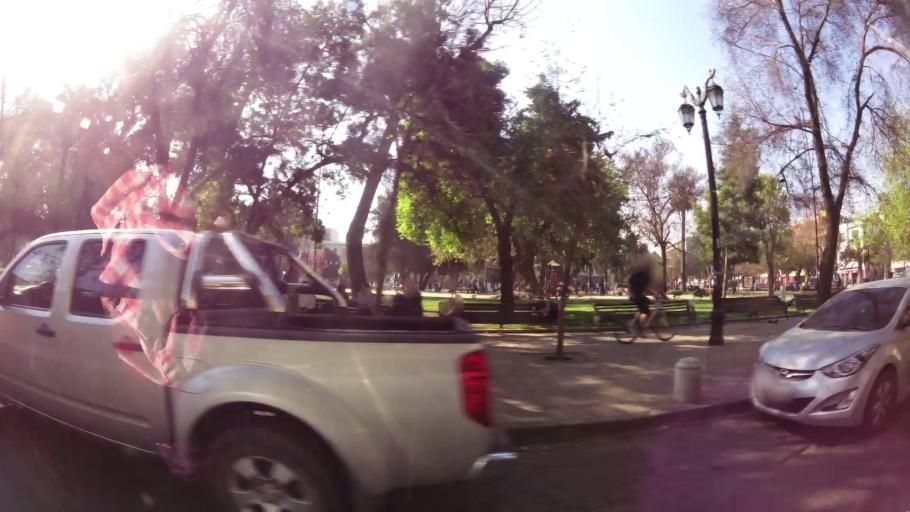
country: CL
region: Santiago Metropolitan
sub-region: Provincia de Santiago
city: Santiago
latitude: -33.4411
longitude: -70.6656
